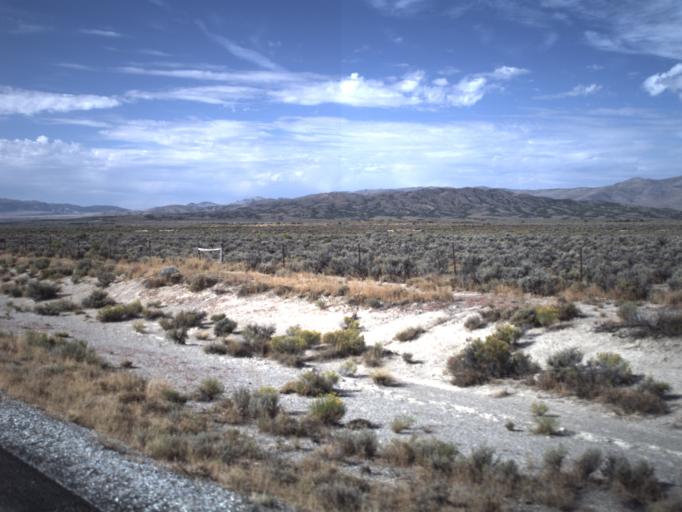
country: US
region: Idaho
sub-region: Cassia County
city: Burley
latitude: 41.6934
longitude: -113.5362
